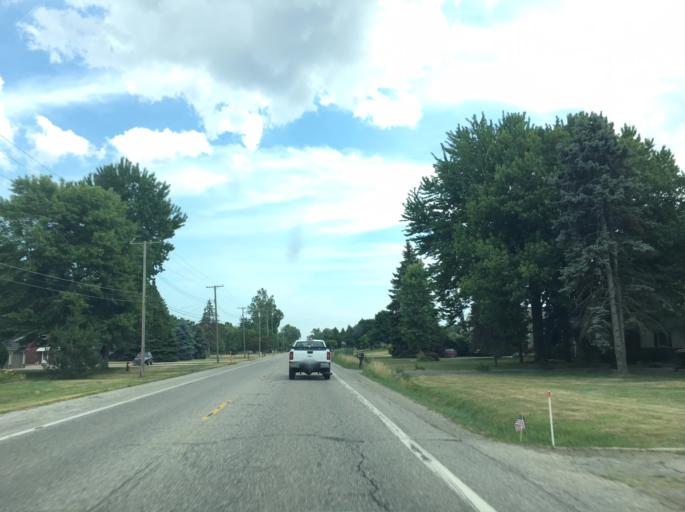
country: US
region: Michigan
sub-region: Macomb County
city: Utica
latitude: 42.6064
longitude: -83.0270
